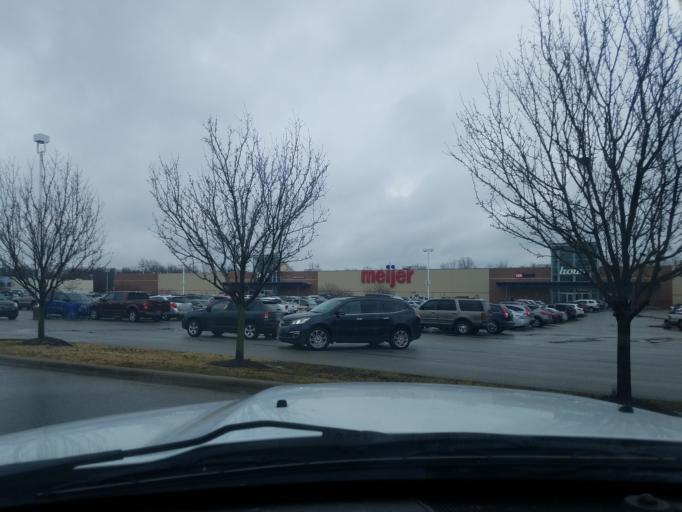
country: US
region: Indiana
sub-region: Clark County
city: Sellersburg
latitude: 38.3495
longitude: -85.7950
